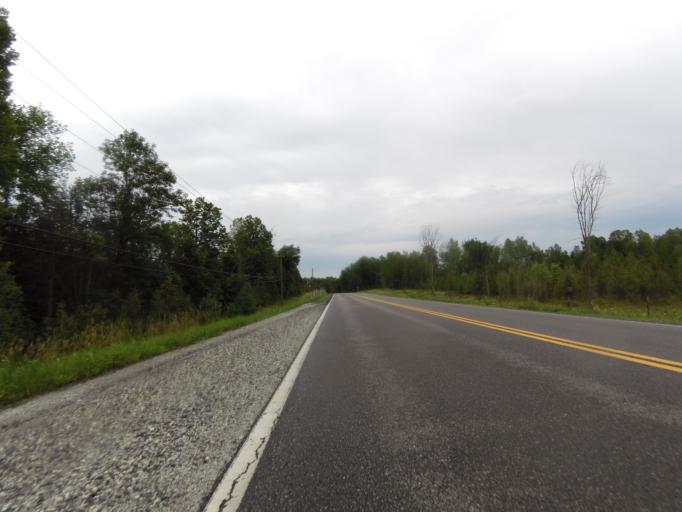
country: CA
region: Ontario
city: Perth
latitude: 45.0286
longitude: -76.3846
